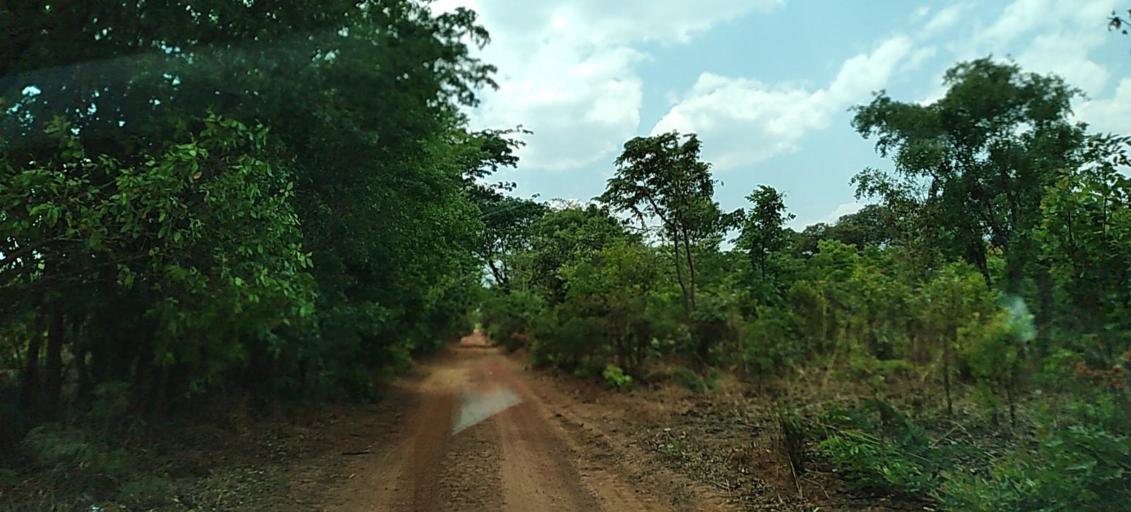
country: ZM
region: Copperbelt
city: Chingola
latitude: -12.5363
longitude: 27.6322
